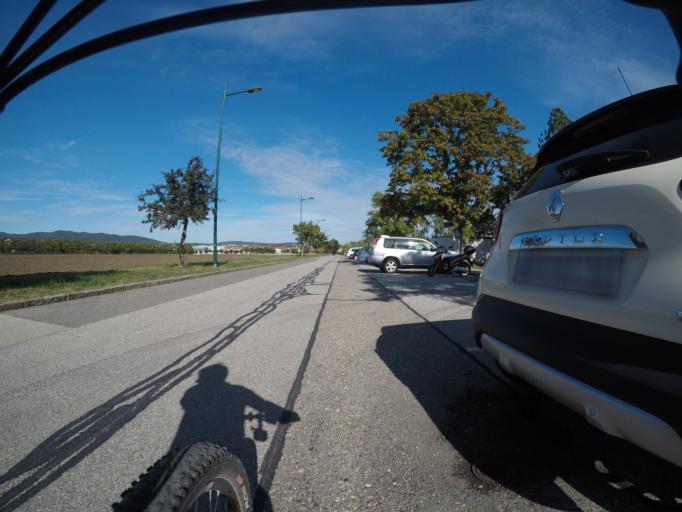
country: AT
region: Lower Austria
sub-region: Politischer Bezirk Modling
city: Modling
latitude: 48.0975
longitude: 16.3021
